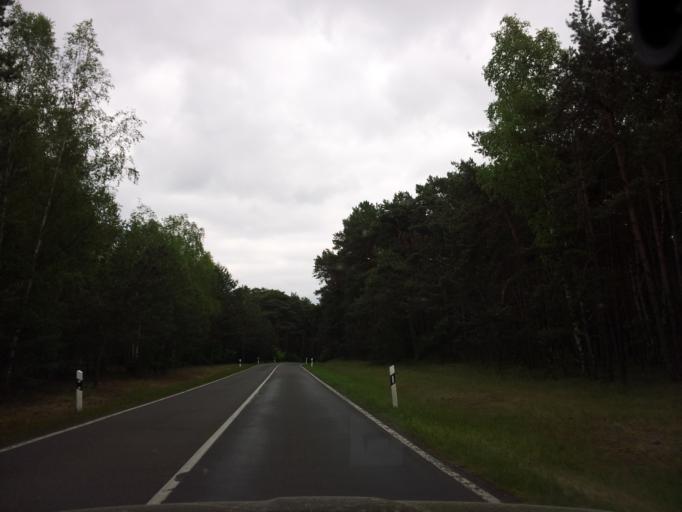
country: DE
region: Brandenburg
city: Treuenbrietzen
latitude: 52.1459
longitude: 12.9407
